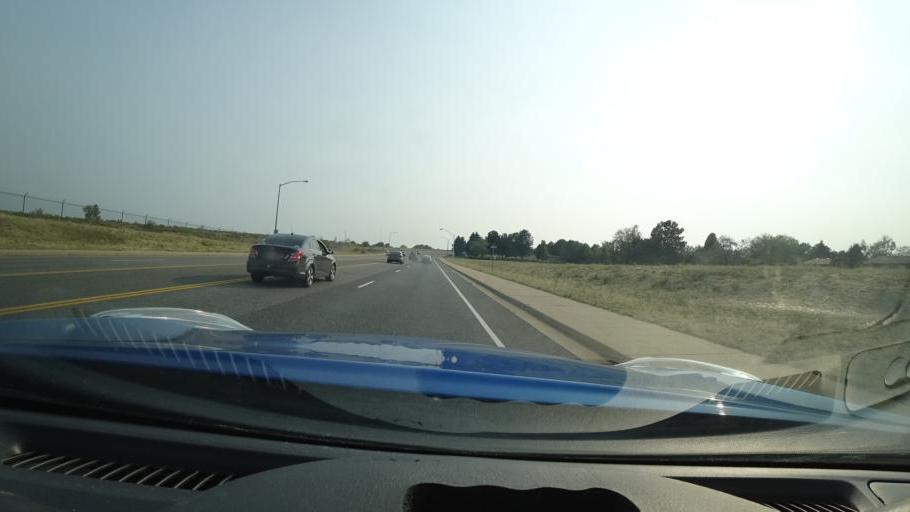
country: US
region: Colorado
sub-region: Adams County
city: Aurora
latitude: 39.6696
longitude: -104.8134
